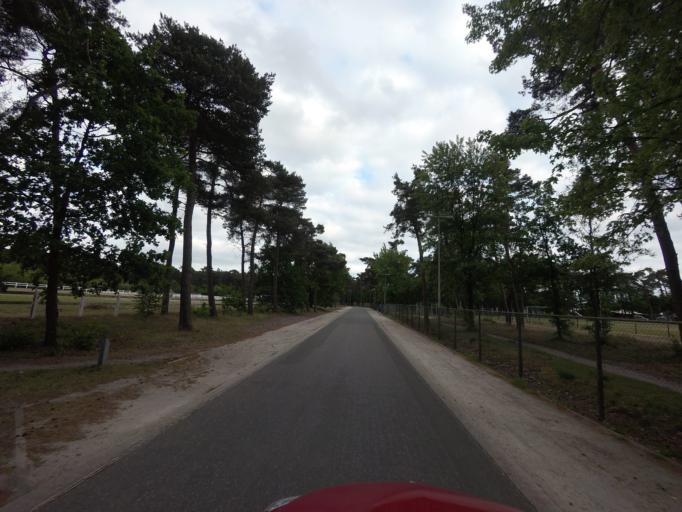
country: BE
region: Flanders
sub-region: Provincie Limburg
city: Lommel
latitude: 51.2492
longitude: 5.3053
